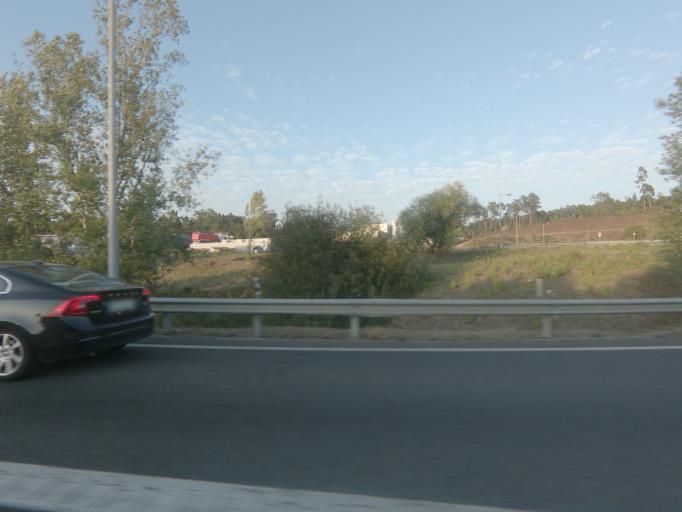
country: PT
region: Leiria
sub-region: Leiria
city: Caranguejeira
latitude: 39.7144
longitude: -8.7114
